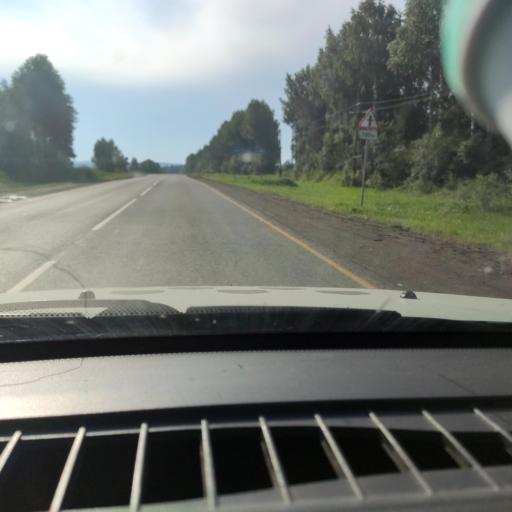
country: RU
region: Kirov
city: Kostino
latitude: 58.8586
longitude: 53.1805
